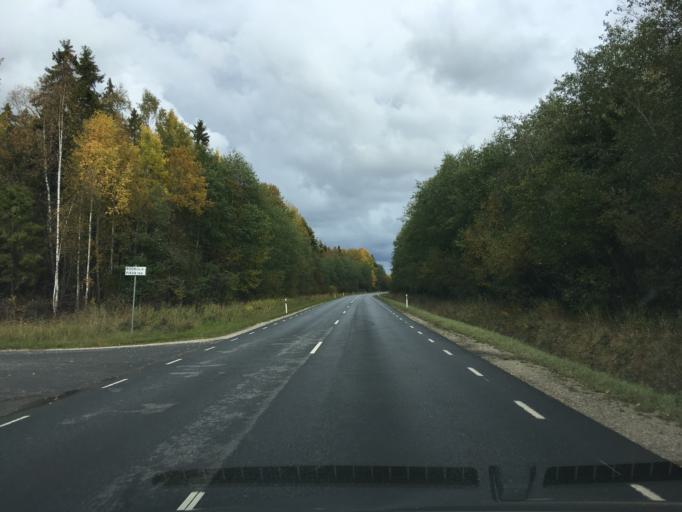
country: EE
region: Harju
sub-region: Anija vald
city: Kehra
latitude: 59.2704
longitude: 25.3562
